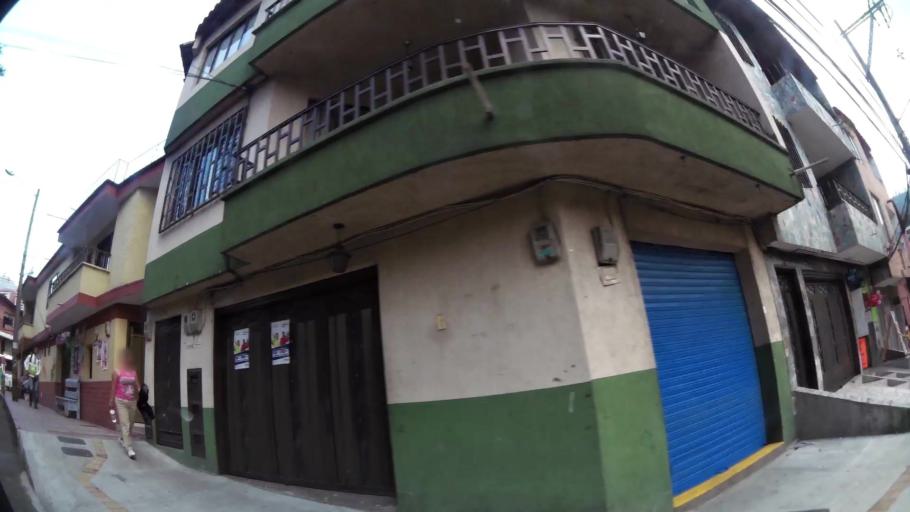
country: CO
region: Antioquia
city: Envigado
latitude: 6.1611
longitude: -75.5821
